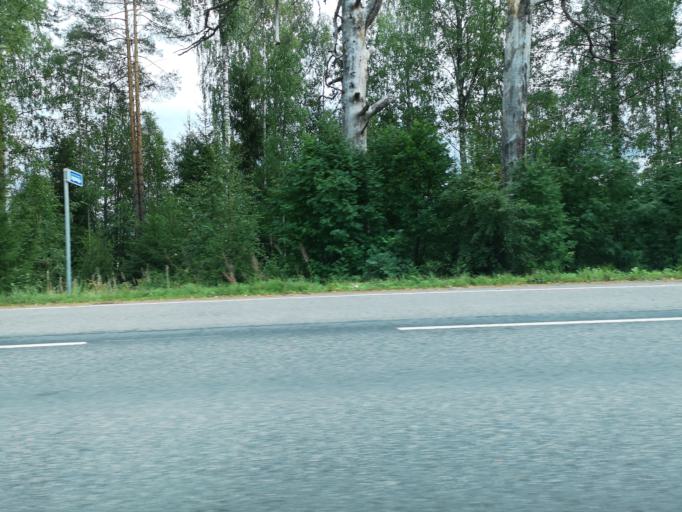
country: FI
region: Central Finland
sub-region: Jyvaeskylae
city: Hankasalmi
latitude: 62.3734
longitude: 26.4423
